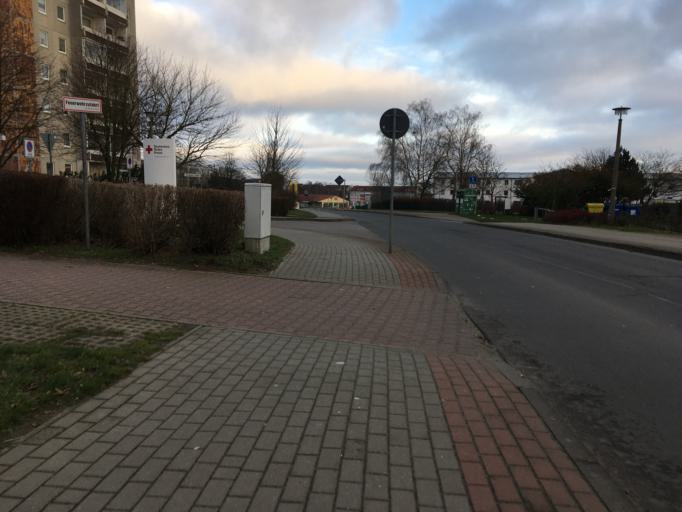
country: DE
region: Mecklenburg-Vorpommern
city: Sassnitz
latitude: 54.5106
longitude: 13.6149
